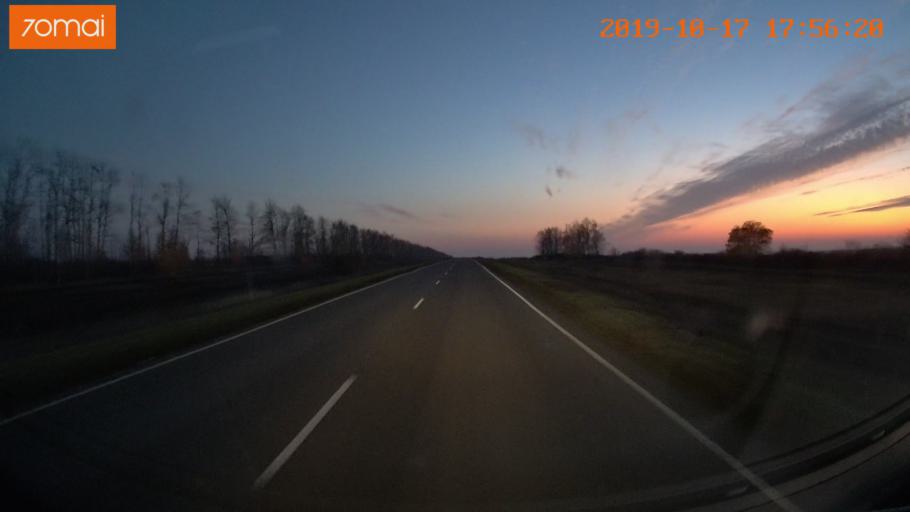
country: RU
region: Tula
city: Kurkino
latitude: 53.5807
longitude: 38.6478
